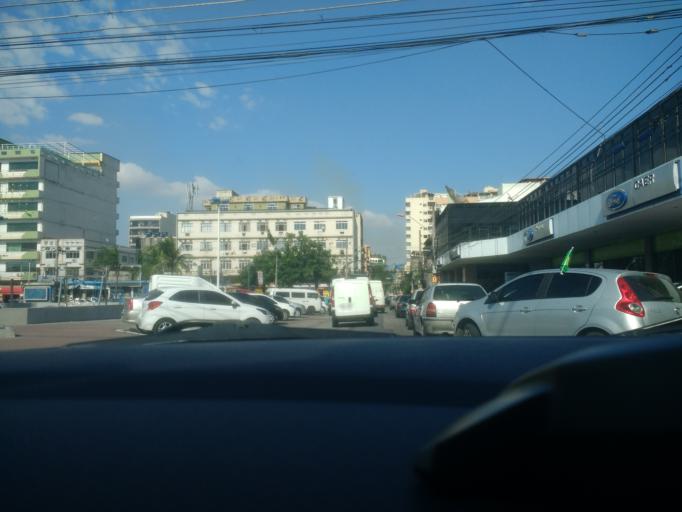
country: BR
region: Rio de Janeiro
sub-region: Duque De Caxias
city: Duque de Caxias
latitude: -22.7917
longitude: -43.3016
